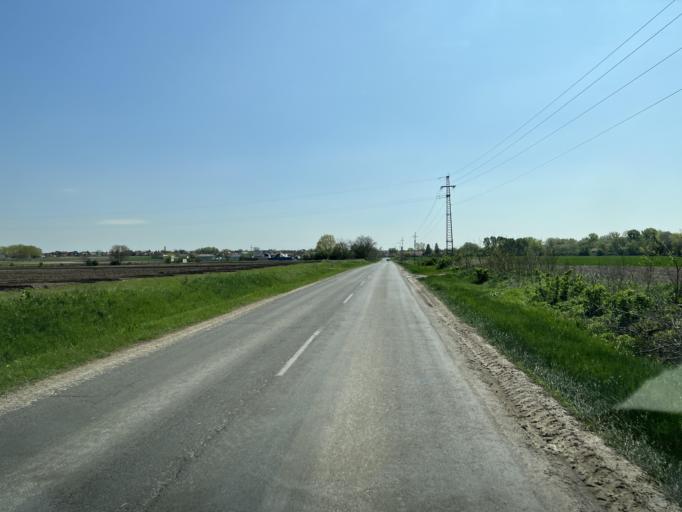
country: HU
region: Pest
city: Ocsa
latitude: 47.3011
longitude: 19.2041
